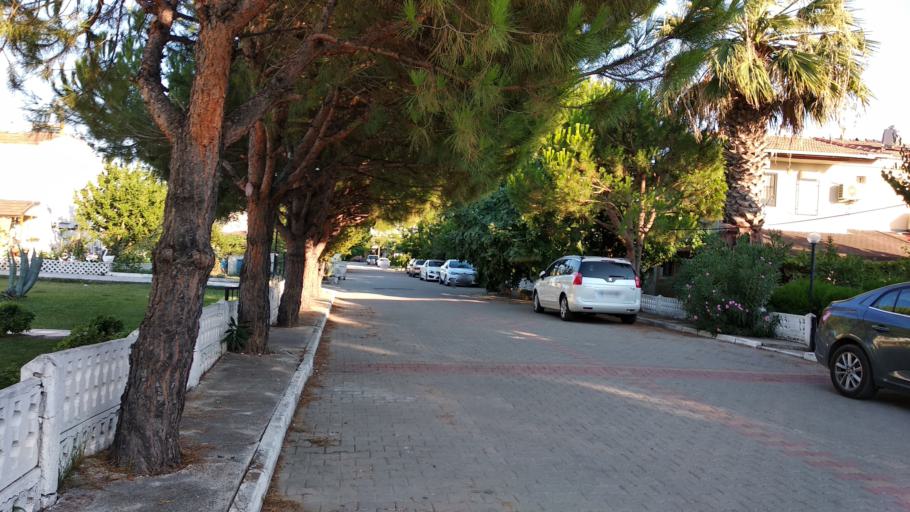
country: TR
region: Balikesir
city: Altinova
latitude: 39.1580
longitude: 26.8203
